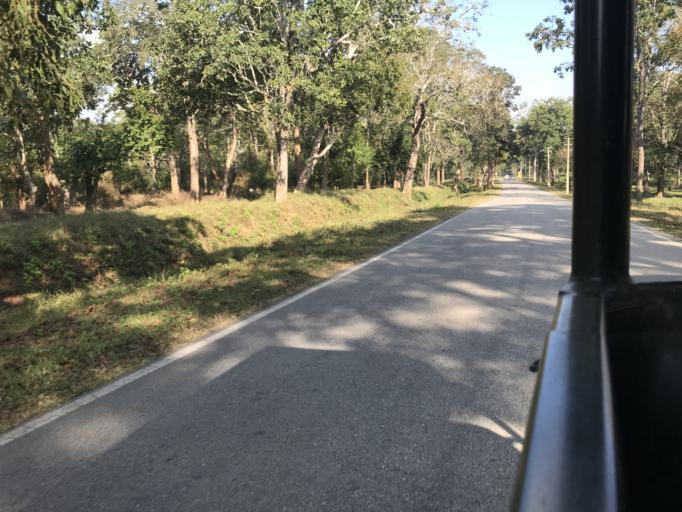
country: IN
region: Karnataka
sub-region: Mysore
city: Heggadadevankote
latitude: 11.9512
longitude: 76.2291
